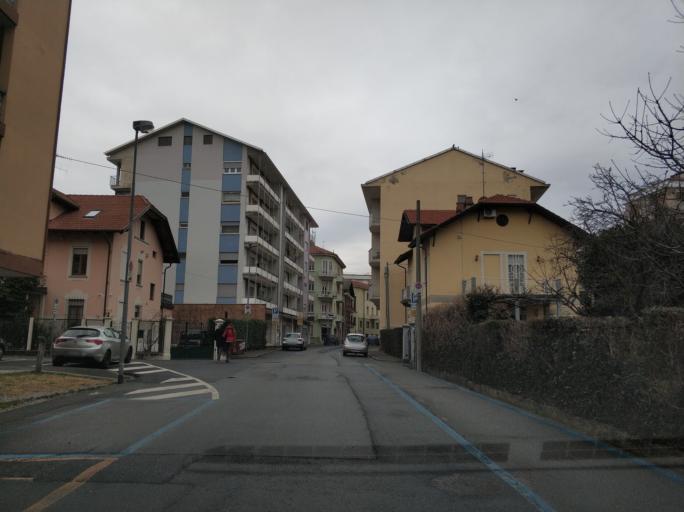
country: IT
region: Piedmont
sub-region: Provincia di Torino
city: Ivrea
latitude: 45.4615
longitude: 7.8737
